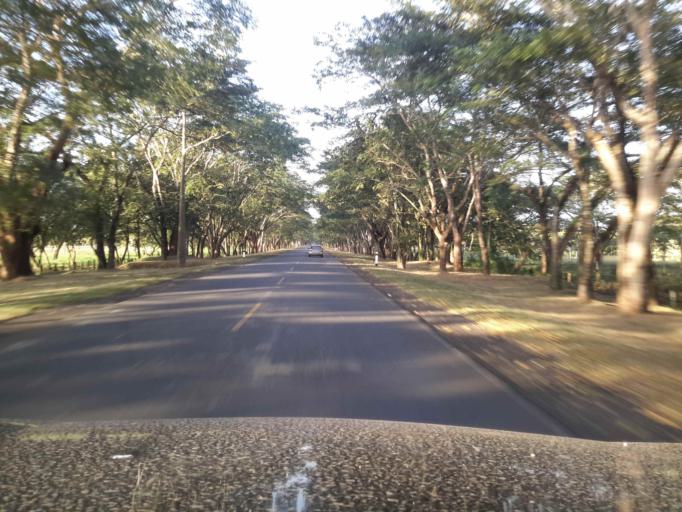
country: NI
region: Rio San Juan
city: San Miguelito
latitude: 11.4480
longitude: -84.8511
